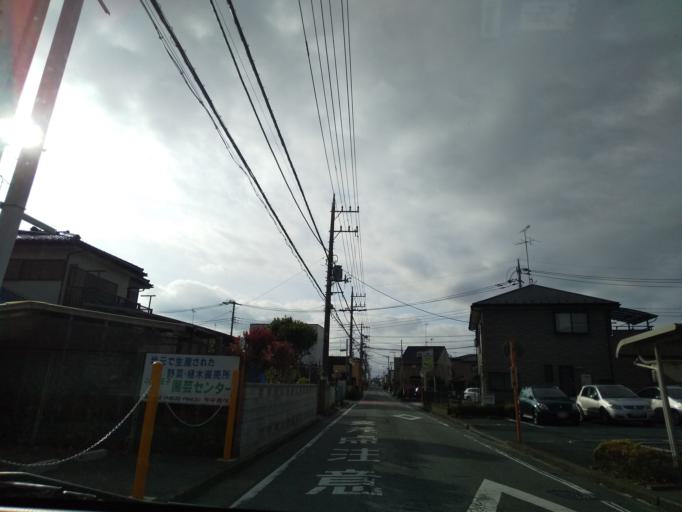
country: JP
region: Tokyo
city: Hachioji
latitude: 35.6858
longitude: 139.3108
